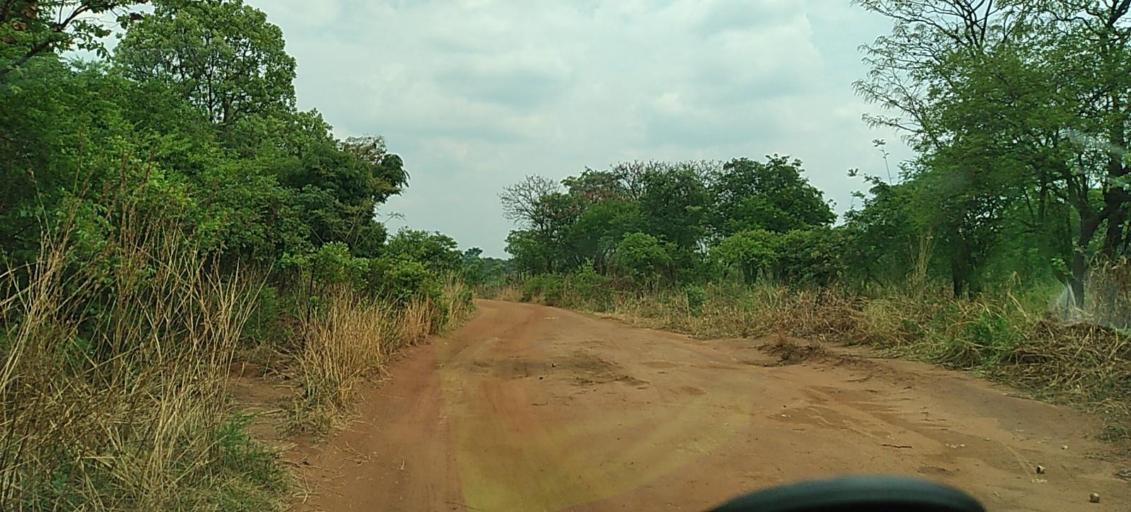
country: ZM
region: North-Western
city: Kansanshi
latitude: -12.0492
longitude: 26.3760
